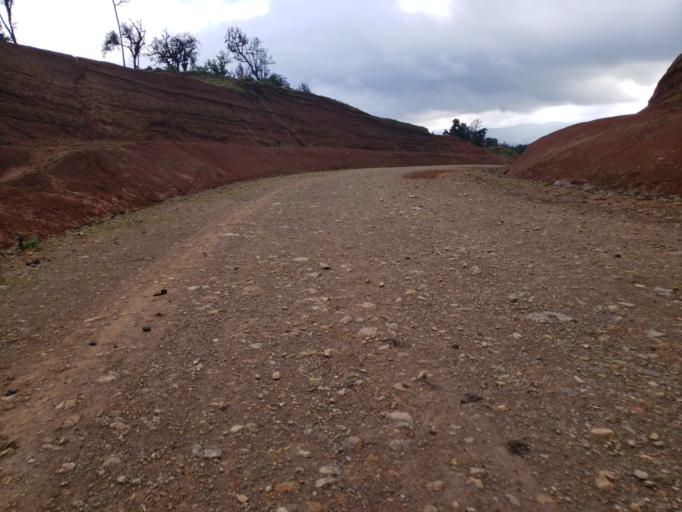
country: ET
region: Oromiya
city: Dodola
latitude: 6.6778
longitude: 39.3648
